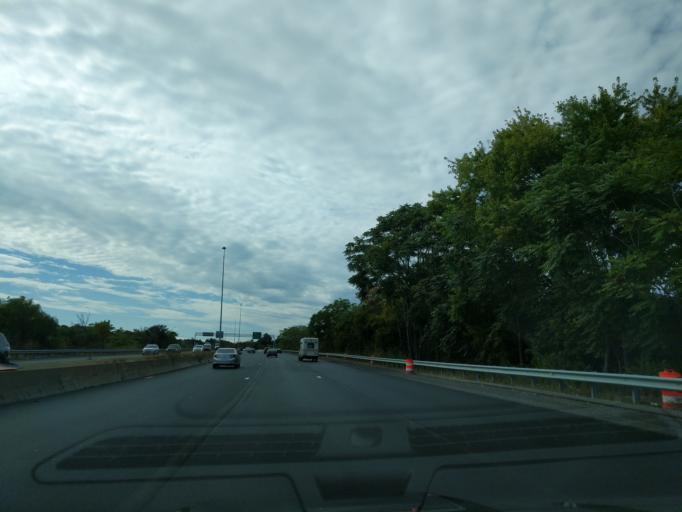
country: US
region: Massachusetts
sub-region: Suffolk County
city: Revere
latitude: 42.4240
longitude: -71.0256
